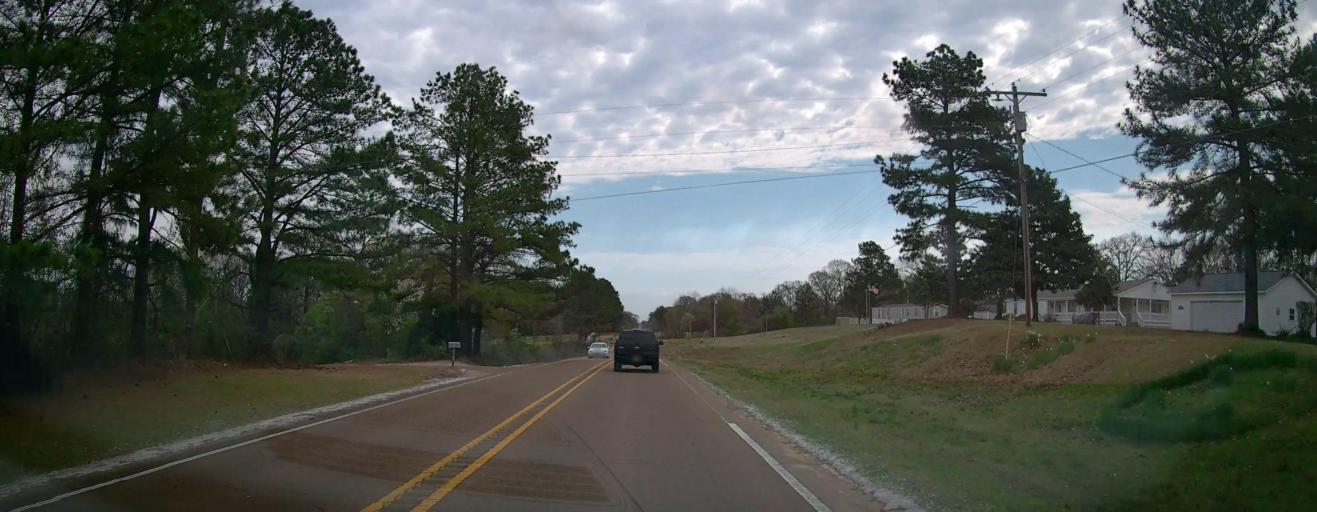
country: US
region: Mississippi
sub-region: Marshall County
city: Byhalia
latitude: 34.8399
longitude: -89.5994
